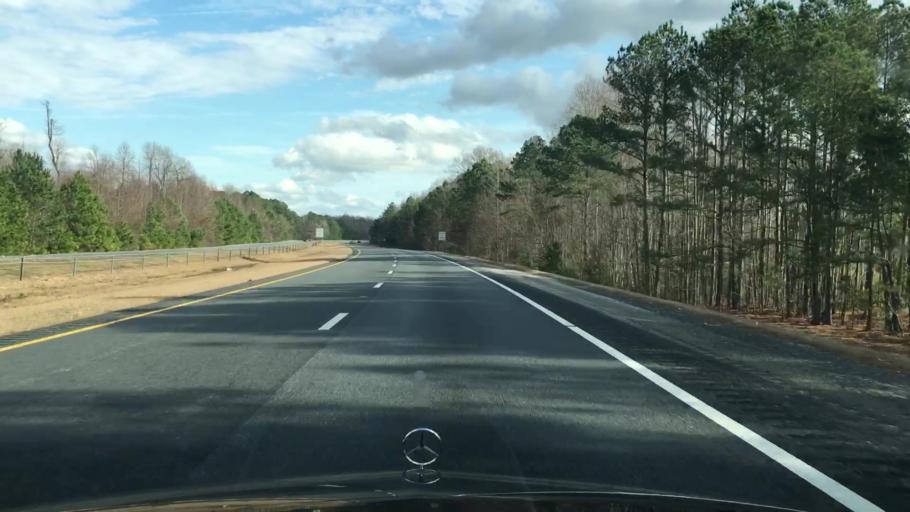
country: US
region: North Carolina
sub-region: Johnston County
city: Four Oaks
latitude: 35.3268
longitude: -78.4387
